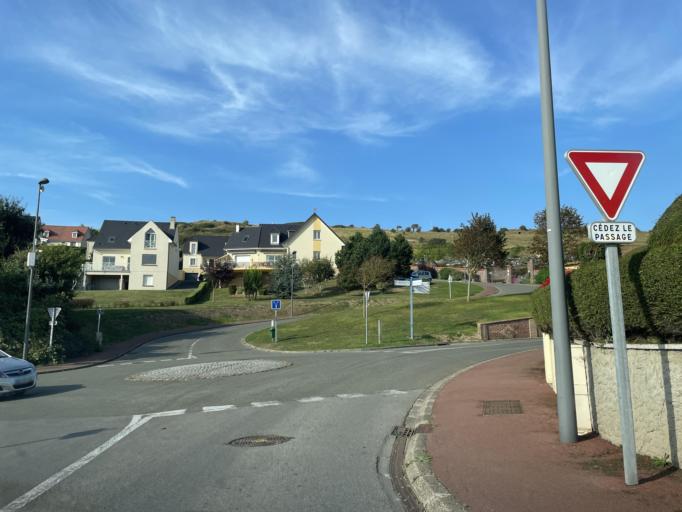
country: FR
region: Picardie
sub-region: Departement de la Somme
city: Mers-les-Bains
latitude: 50.0704
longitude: 1.3923
